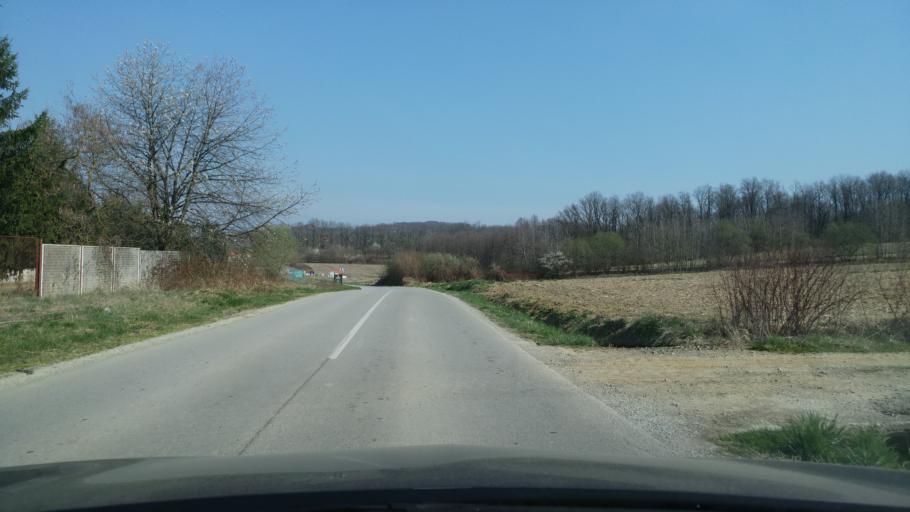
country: HR
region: Zagrebacka
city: Pojatno
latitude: 45.9678
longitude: 15.7373
